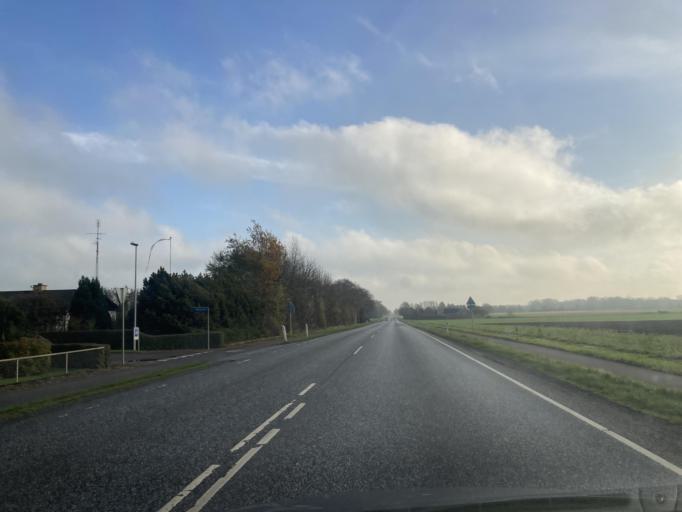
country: DK
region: Zealand
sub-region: Guldborgsund Kommune
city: Sakskobing
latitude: 54.7933
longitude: 11.6628
